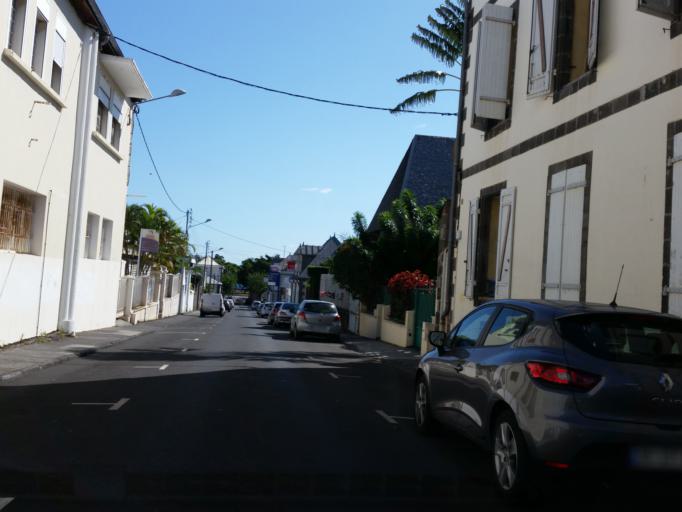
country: RE
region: Reunion
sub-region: Reunion
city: Saint-Denis
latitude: -20.8751
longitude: 55.4489
